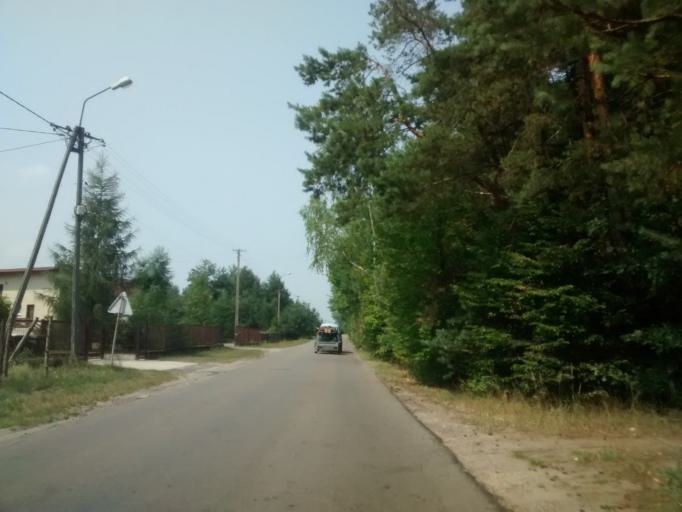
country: PL
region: Lesser Poland Voivodeship
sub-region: Powiat olkuski
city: Klucze
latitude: 50.3625
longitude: 19.5515
